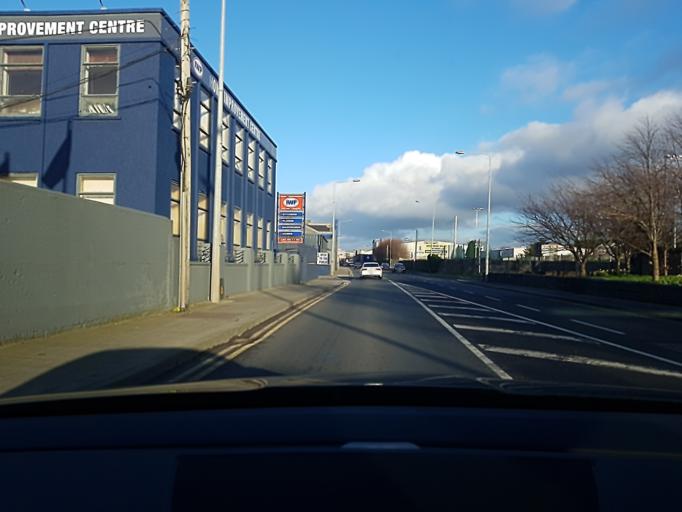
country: IE
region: Munster
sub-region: County Limerick
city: Luimneach
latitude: 52.6564
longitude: -8.6463
